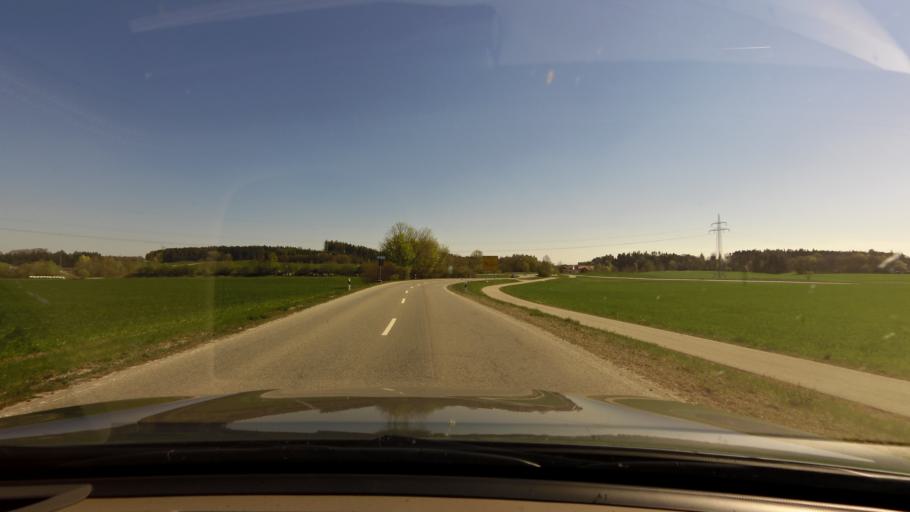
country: DE
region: Bavaria
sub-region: Upper Bavaria
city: Altdorf
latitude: 48.1517
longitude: 12.1828
